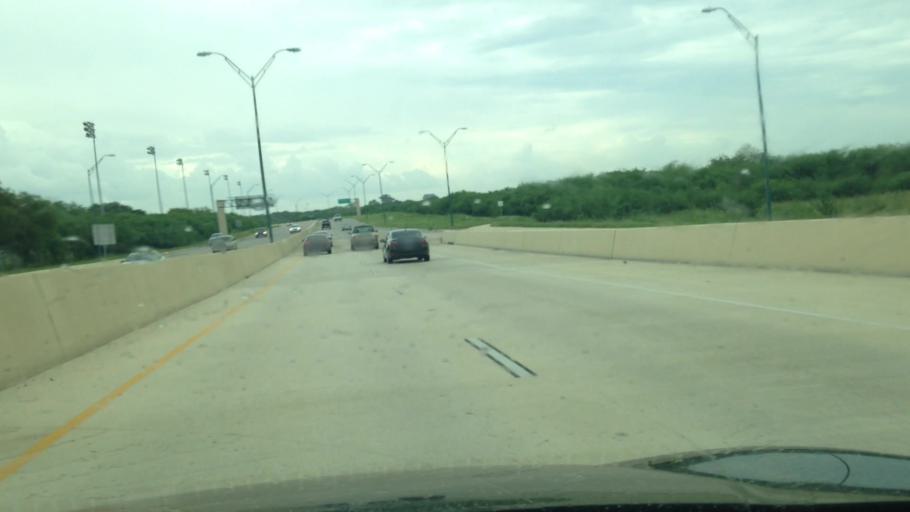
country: US
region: Texas
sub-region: Bexar County
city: Castle Hills
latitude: 29.5472
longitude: -98.4708
